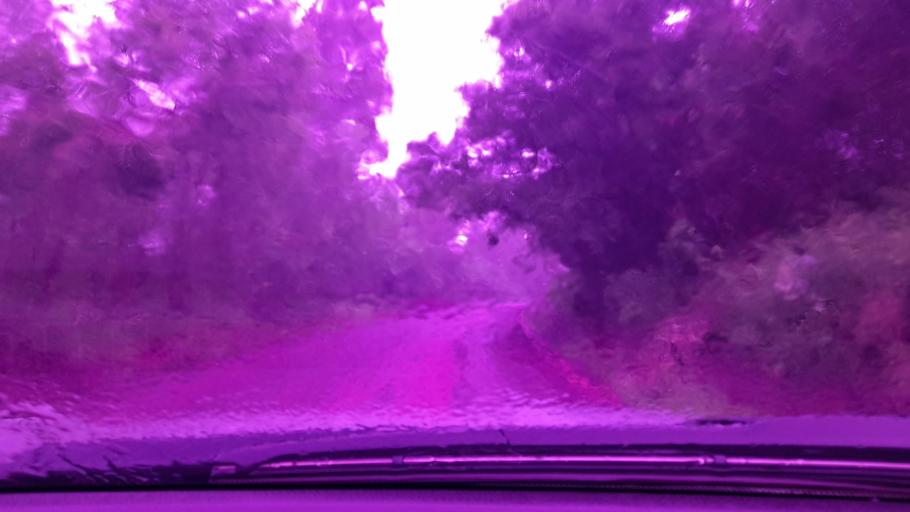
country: ET
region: Oromiya
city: Metu
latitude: 8.3632
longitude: 35.5943
